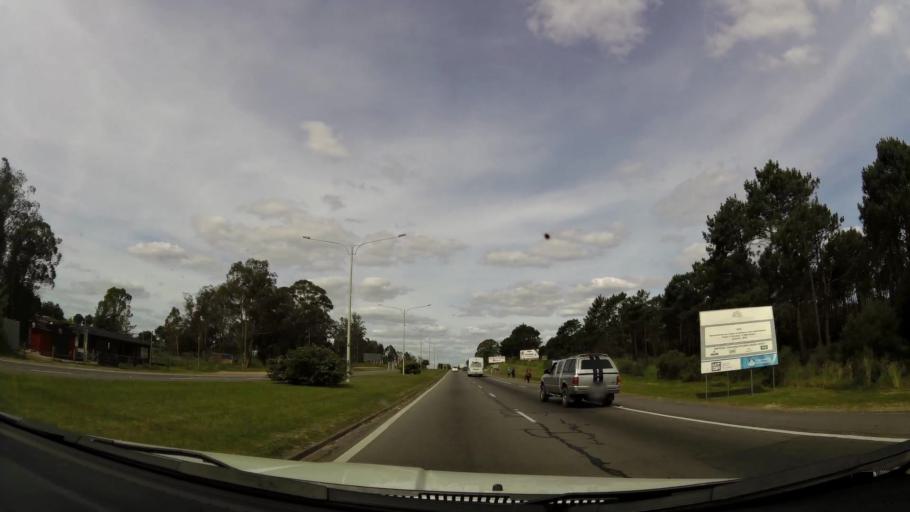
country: UY
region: Canelones
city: Empalme Olmos
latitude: -34.7829
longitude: -55.8828
